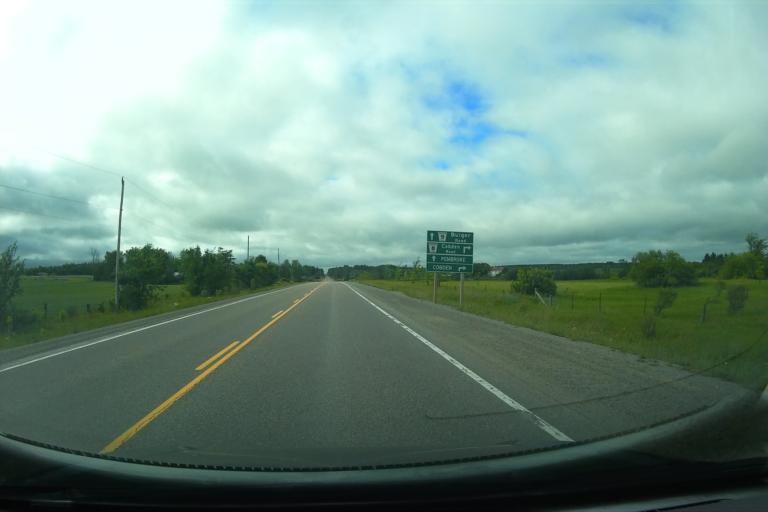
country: CA
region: Ontario
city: Pembroke
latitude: 45.5488
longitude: -76.9971
